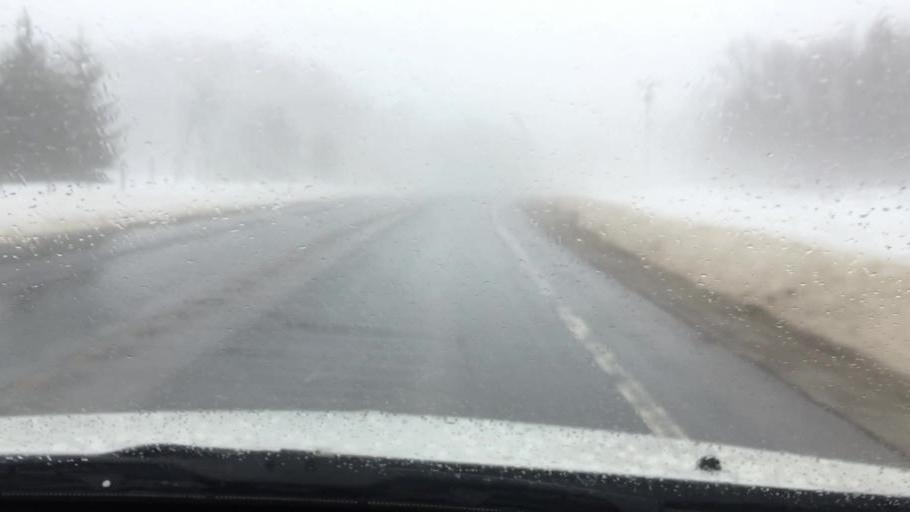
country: US
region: Michigan
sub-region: Antrim County
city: Mancelona
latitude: 44.9465
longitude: -85.0508
